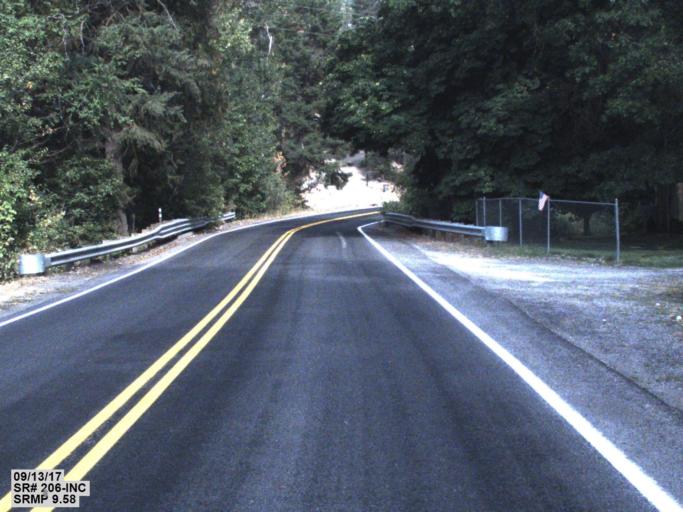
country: US
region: Washington
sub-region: Spokane County
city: Trentwood
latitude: 47.8357
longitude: -117.1965
